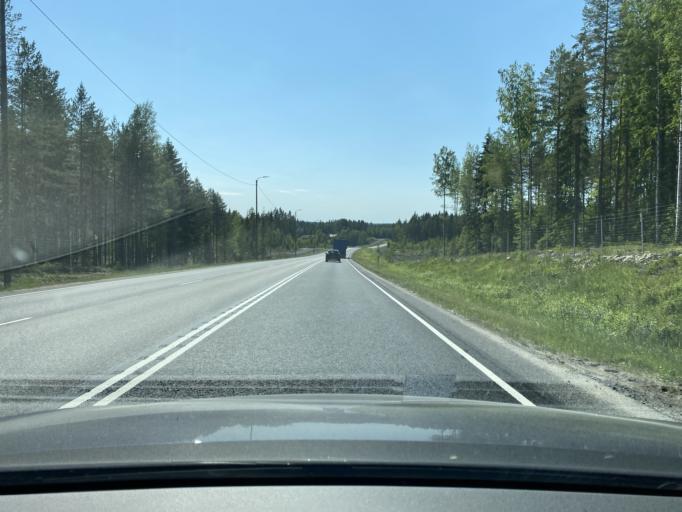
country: FI
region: Pirkanmaa
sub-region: Lounais-Pirkanmaa
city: Mouhijaervi
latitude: 61.3730
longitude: 23.1418
